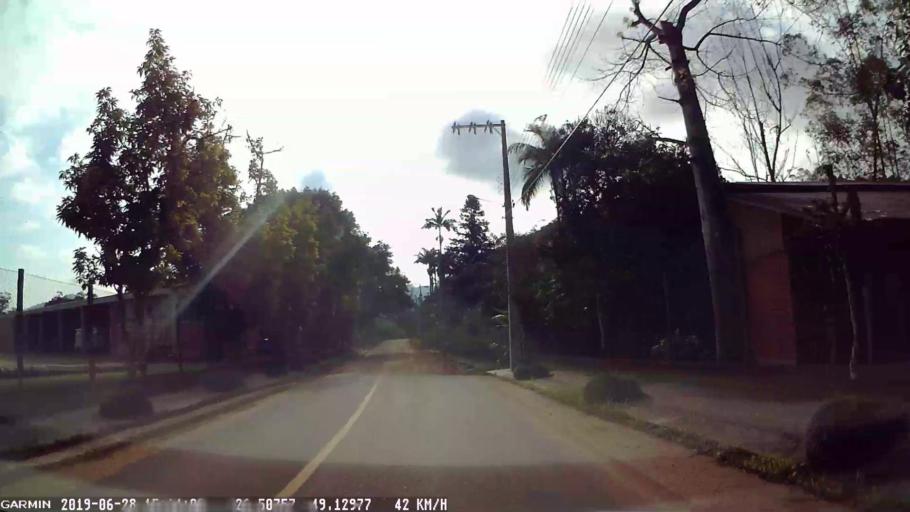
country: BR
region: Santa Catarina
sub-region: Jaragua Do Sul
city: Jaragua do Sul
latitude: -26.5075
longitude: -49.1299
